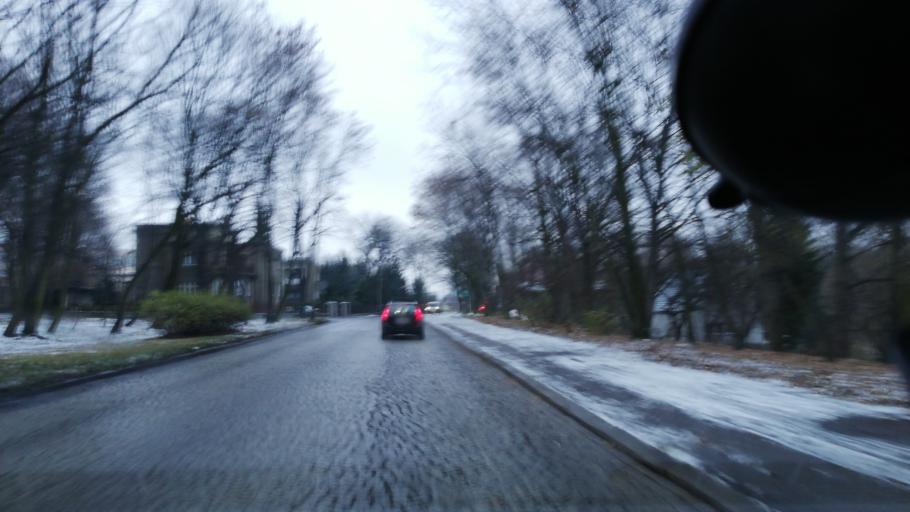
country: PL
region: Silesian Voivodeship
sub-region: Chorzow
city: Chorzow
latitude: 50.2951
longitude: 18.9678
